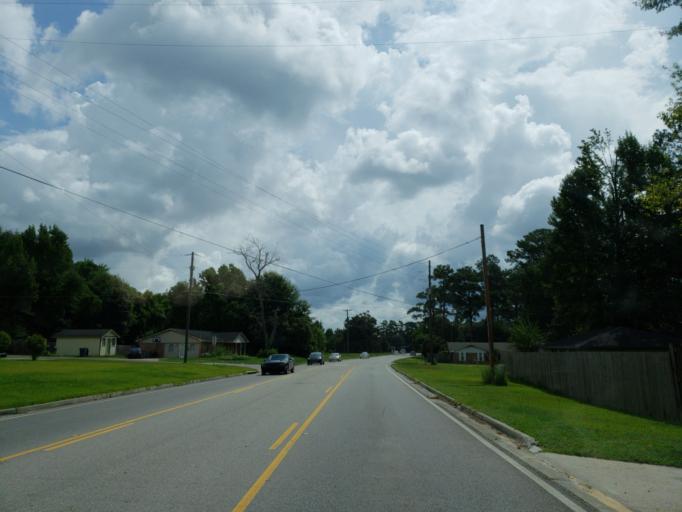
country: US
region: Mississippi
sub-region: Lamar County
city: Arnold Line
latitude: 31.3368
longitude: -89.3609
